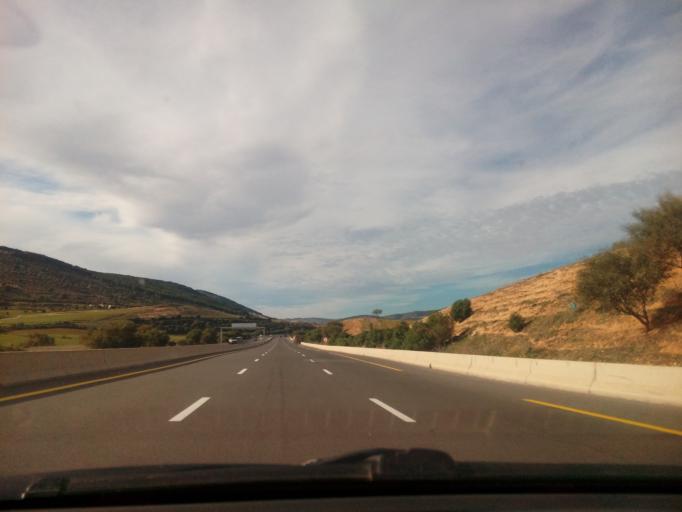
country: DZ
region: Sidi Bel Abbes
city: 'Ain el Berd
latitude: 35.4394
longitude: -0.4222
